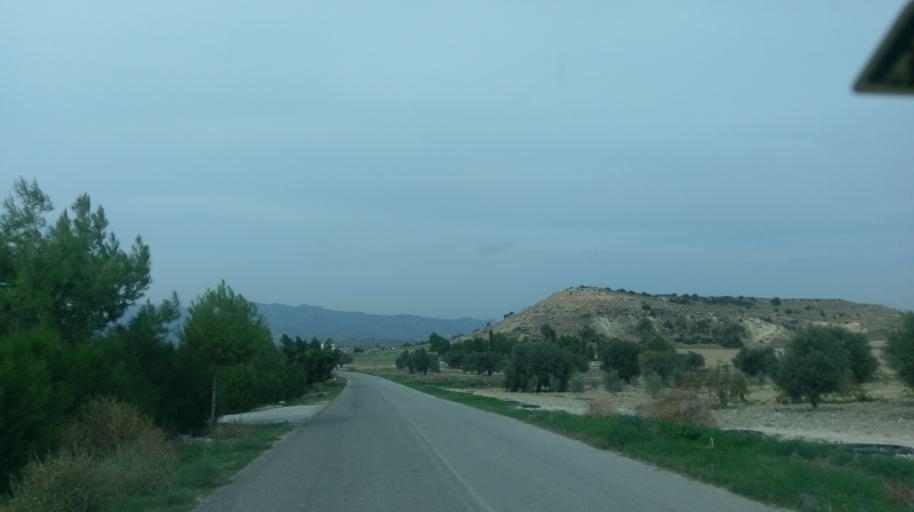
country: CY
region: Ammochostos
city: Trikomo
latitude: 35.3227
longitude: 33.9349
